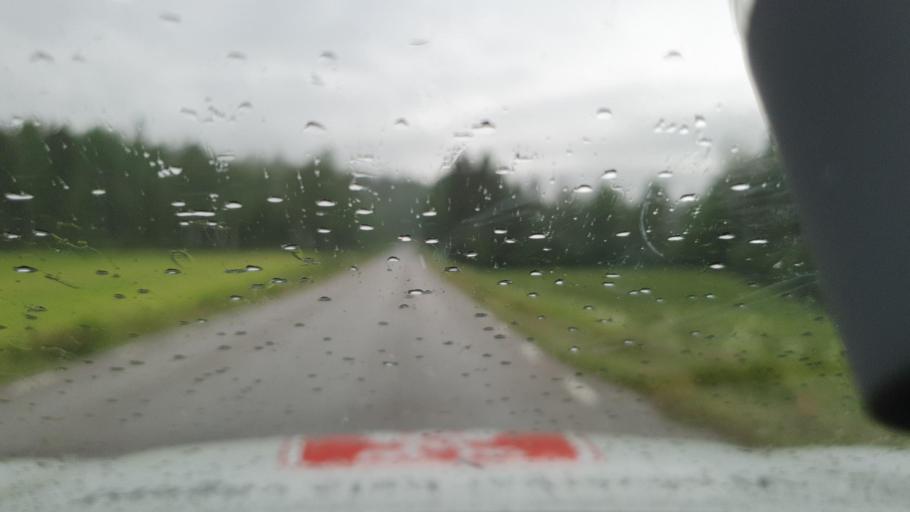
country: SE
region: Vaesterbotten
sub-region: Vannas Kommun
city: Vaennaes
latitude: 63.7896
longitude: 19.5646
